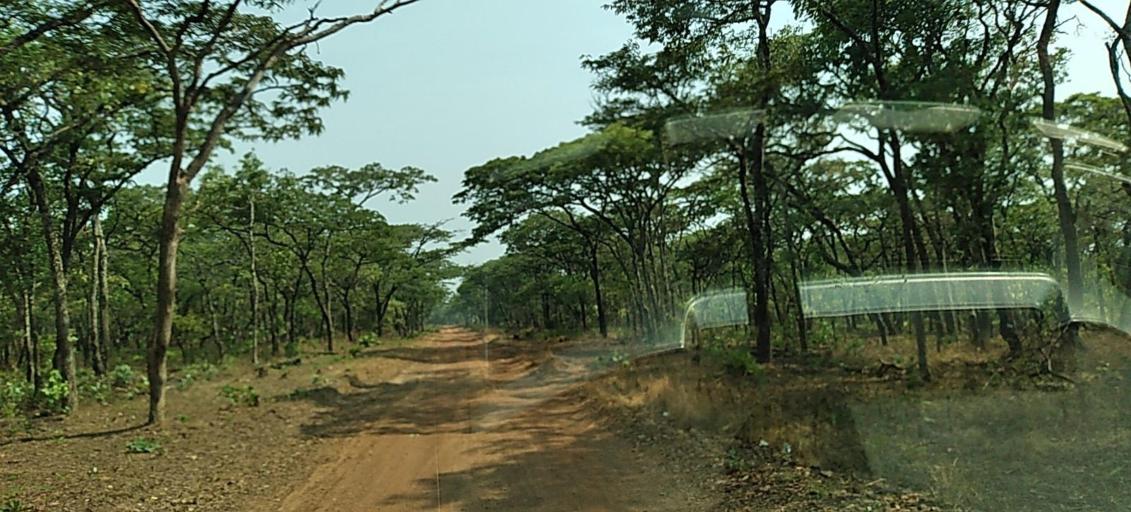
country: ZM
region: North-Western
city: Kansanshi
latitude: -12.0816
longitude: 26.8883
